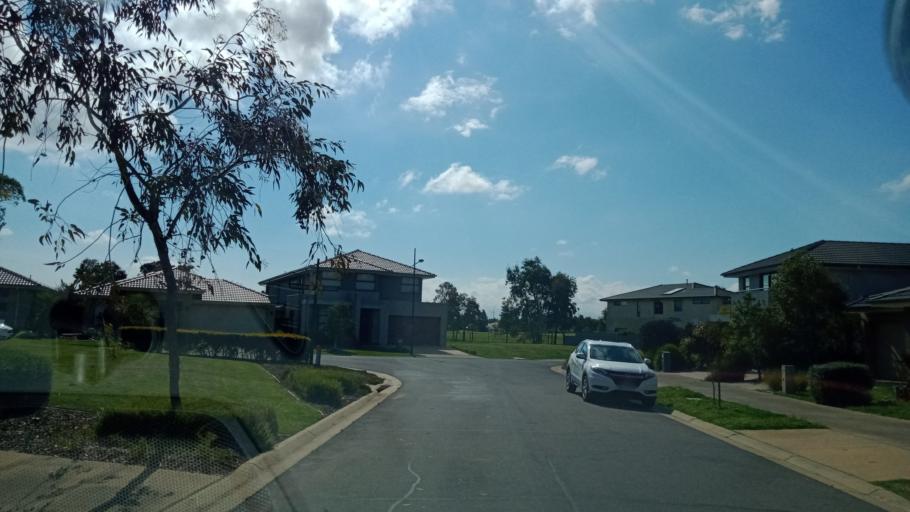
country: AU
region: Victoria
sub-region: Frankston
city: Sandhurst
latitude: -38.0827
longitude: 145.2109
